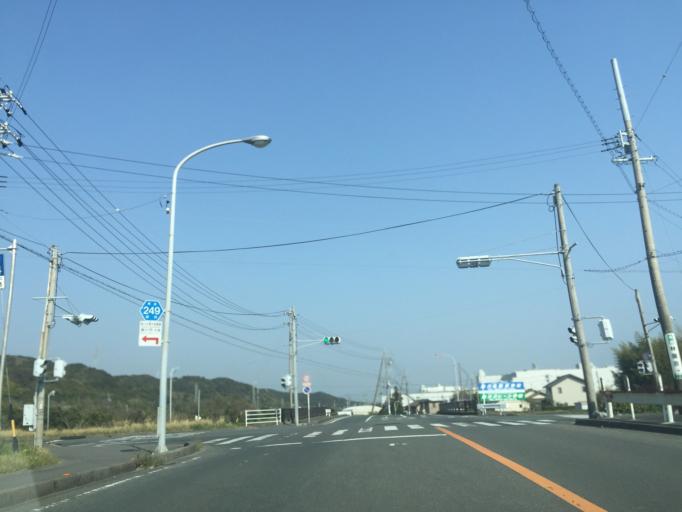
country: JP
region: Shizuoka
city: Kakegawa
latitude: 34.6763
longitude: 138.0058
